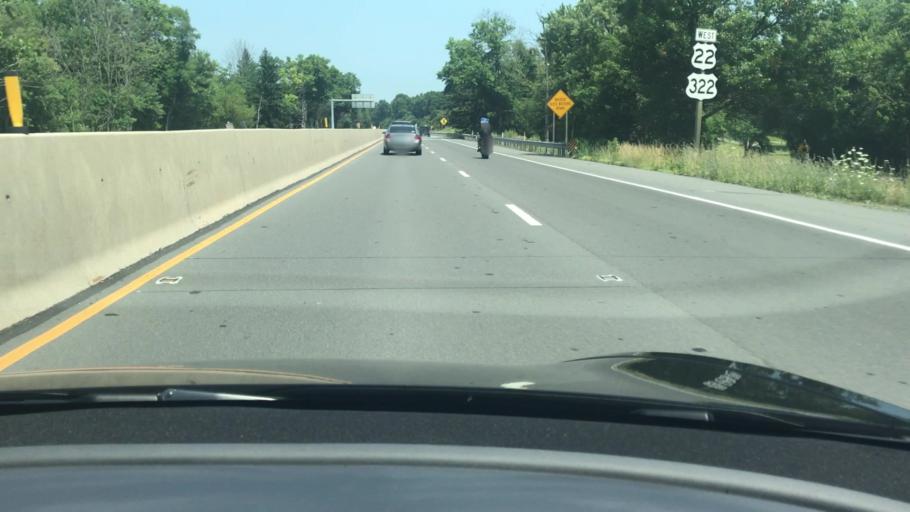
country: US
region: Pennsylvania
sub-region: Perry County
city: Duncannon
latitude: 40.4254
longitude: -77.0105
